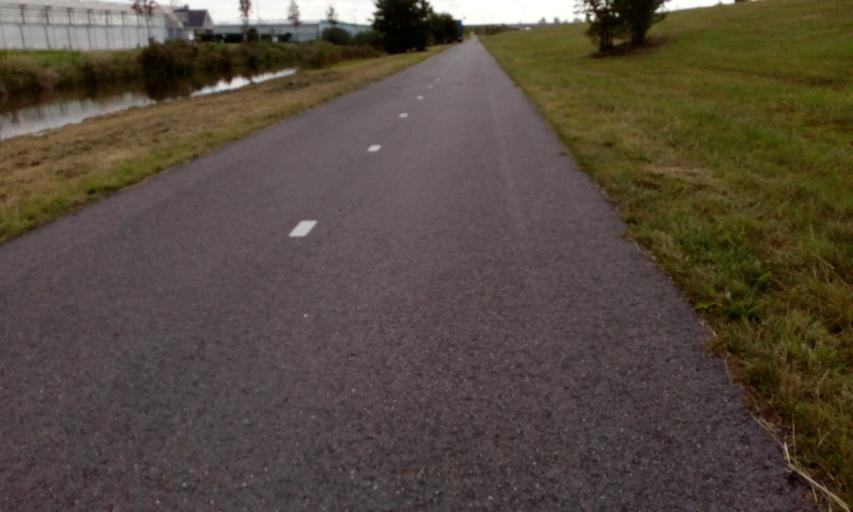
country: NL
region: South Holland
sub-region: Gemeente Westland
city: Kwintsheul
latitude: 52.0068
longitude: 4.2749
